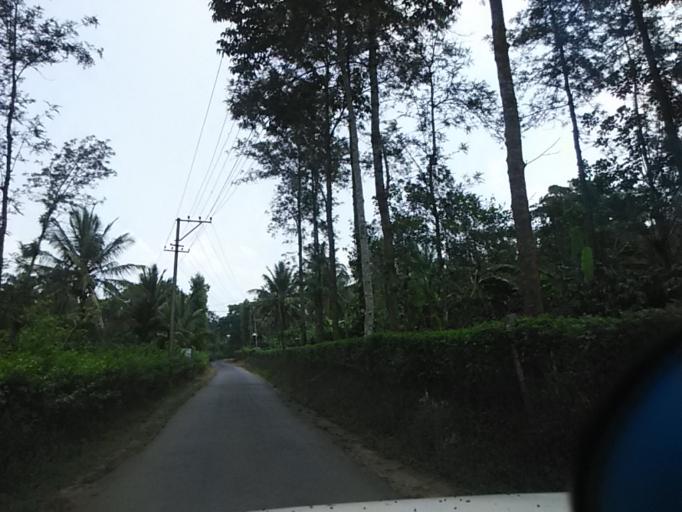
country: IN
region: Karnataka
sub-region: Kodagu
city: Virarajendrapet
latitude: 12.2119
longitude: 75.7360
